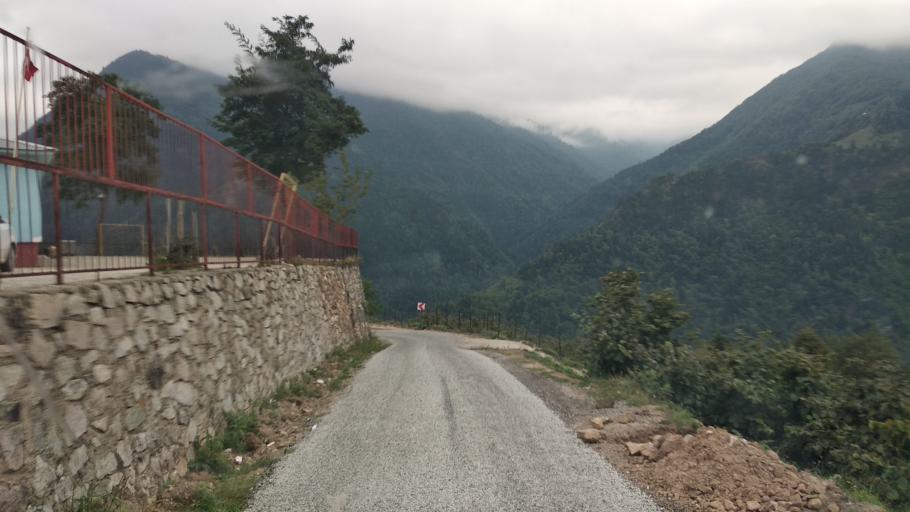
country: TR
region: Giresun
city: Dogankent
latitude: 40.7435
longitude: 38.9914
